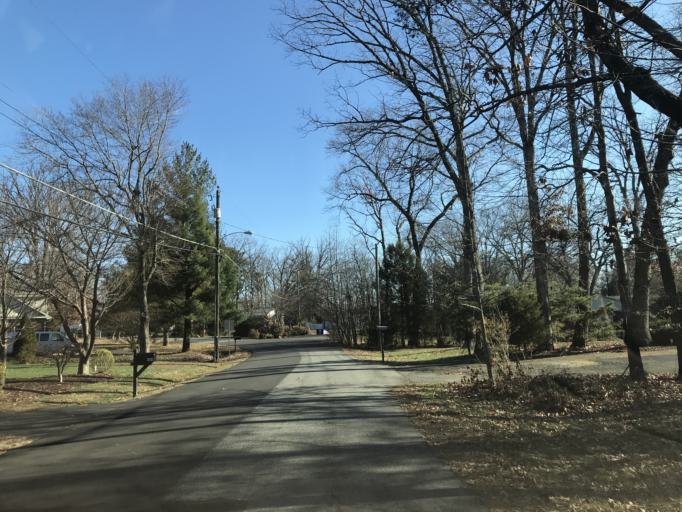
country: US
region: Virginia
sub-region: Fairfax County
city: Franconia
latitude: 38.7764
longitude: -77.1636
